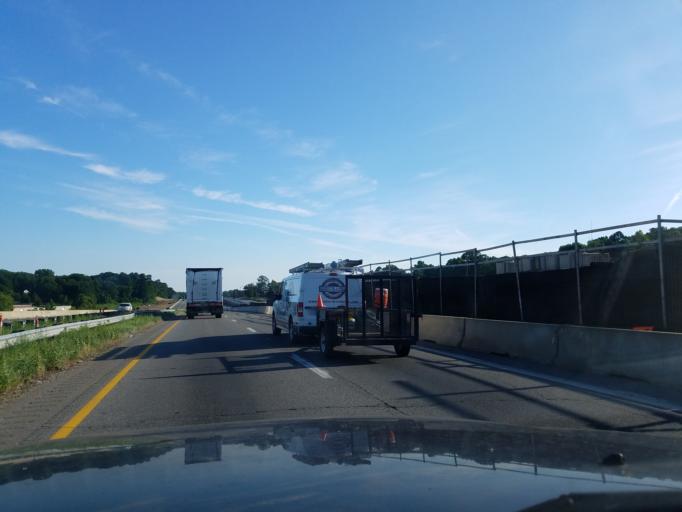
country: US
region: North Carolina
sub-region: Durham County
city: Durham
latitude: 35.9915
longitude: -78.8628
